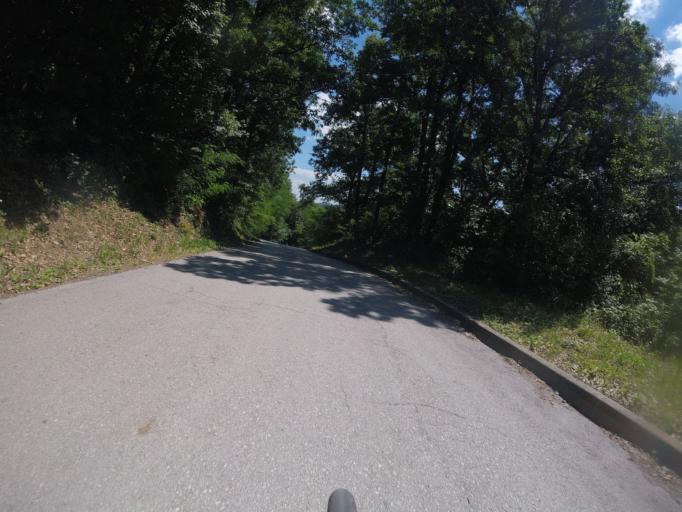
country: HR
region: Karlovacka
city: Ozalj
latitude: 45.6846
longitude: 15.4114
